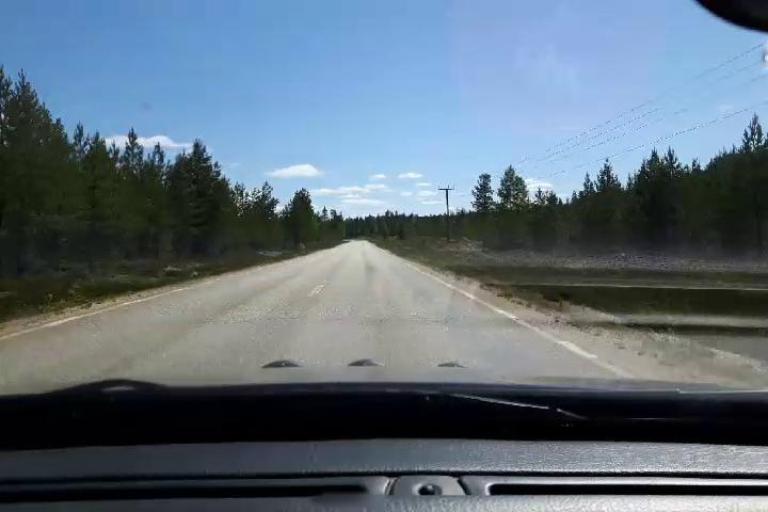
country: SE
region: Jaemtland
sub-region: Harjedalens Kommun
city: Sveg
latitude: 62.1064
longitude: 15.0653
